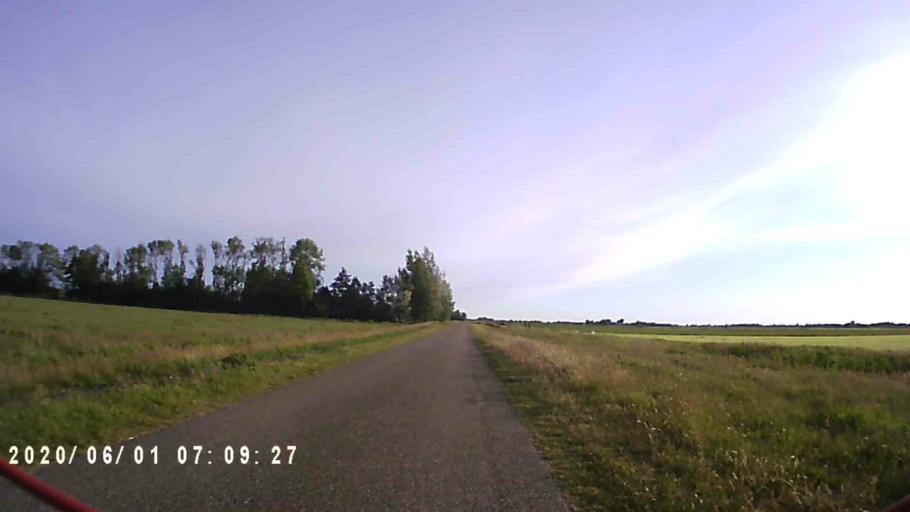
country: NL
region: Friesland
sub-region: Gemeente Dantumadiel
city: Walterswald
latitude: 53.3053
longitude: 6.0719
